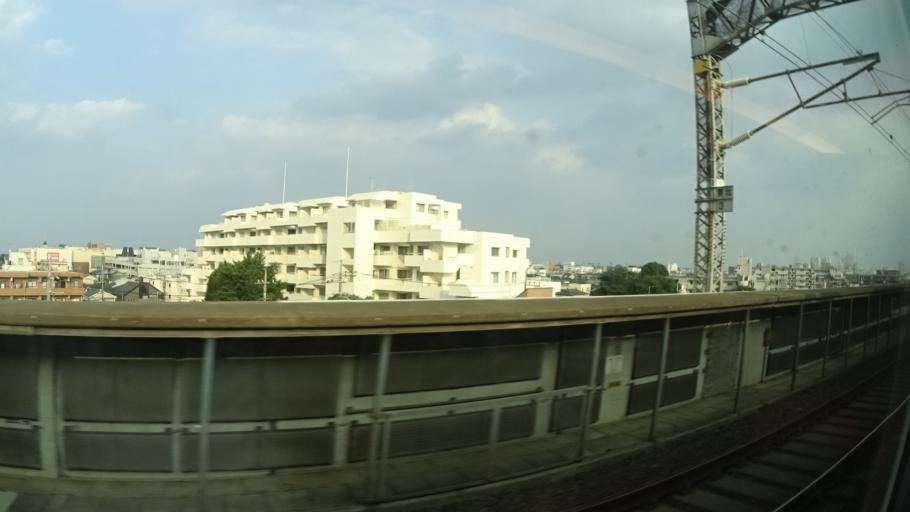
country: JP
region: Saitama
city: Ageoshimo
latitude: 35.9298
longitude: 139.6163
